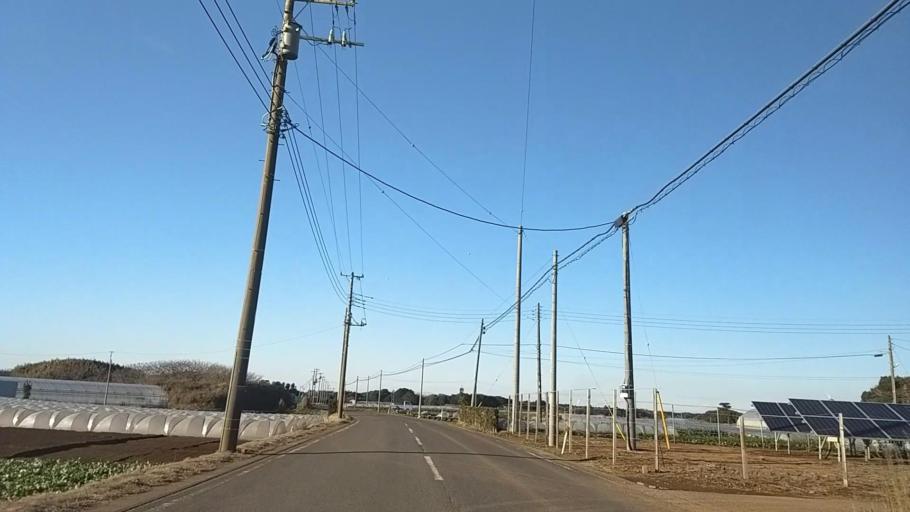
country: JP
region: Chiba
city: Asahi
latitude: 35.7386
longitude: 140.7374
